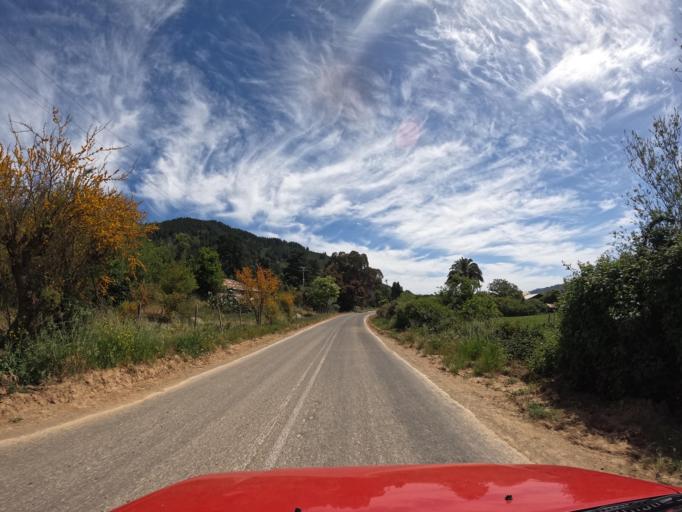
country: CL
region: Maule
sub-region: Provincia de Talca
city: Talca
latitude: -34.9891
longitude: -71.8197
